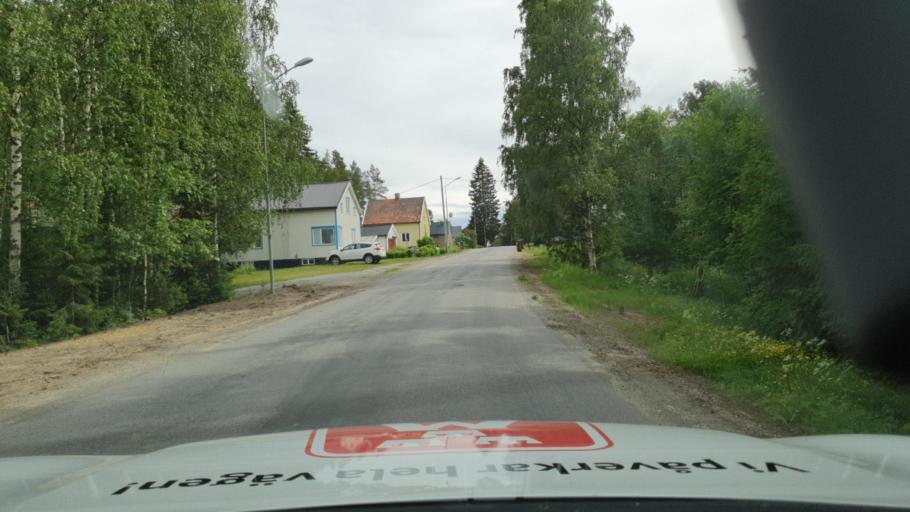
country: SE
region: Vaesterbotten
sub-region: Robertsfors Kommun
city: Robertsfors
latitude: 64.4089
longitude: 21.0040
